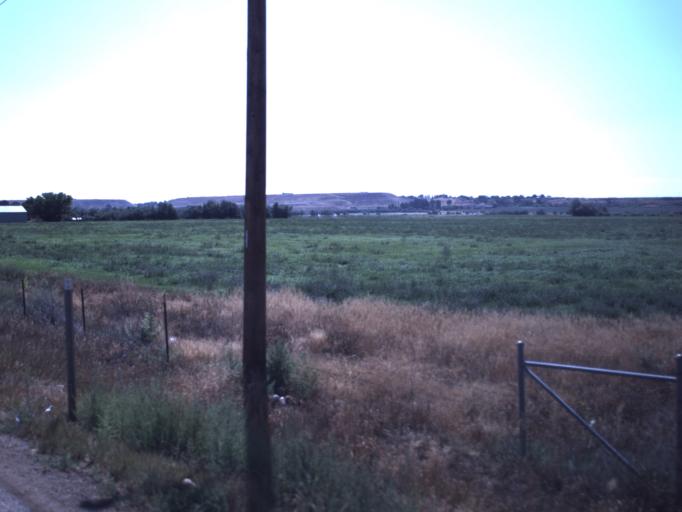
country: US
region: Utah
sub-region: Duchesne County
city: Roosevelt
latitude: 40.2582
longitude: -110.1229
